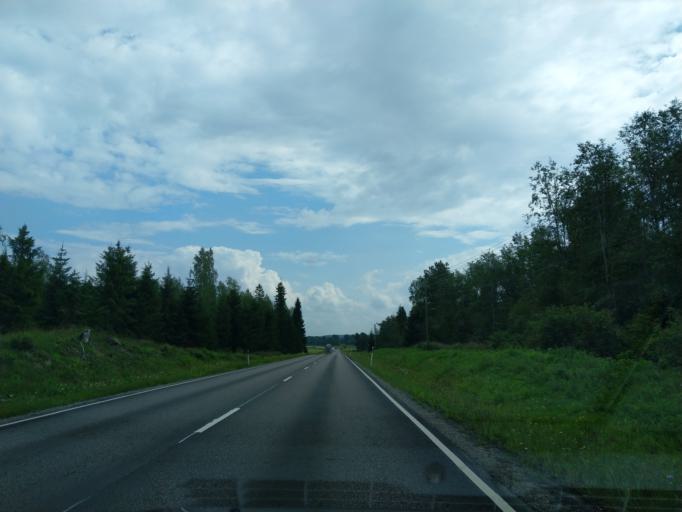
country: FI
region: South Karelia
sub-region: Imatra
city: Parikkala
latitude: 61.6094
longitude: 29.4573
